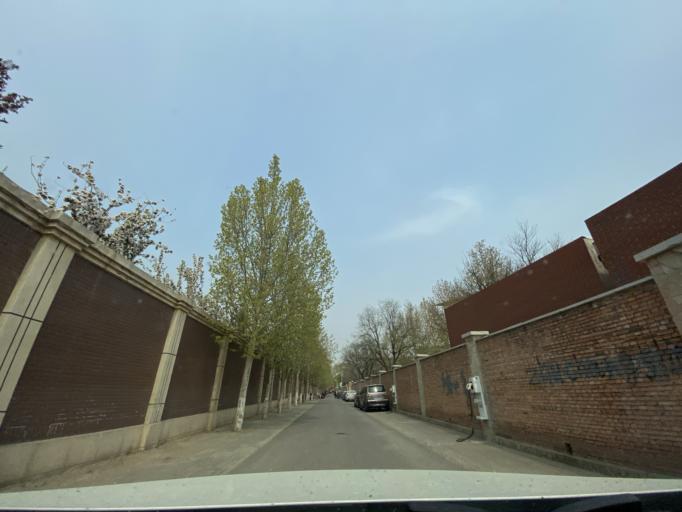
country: CN
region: Beijing
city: Sijiqing
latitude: 39.9409
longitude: 116.2457
